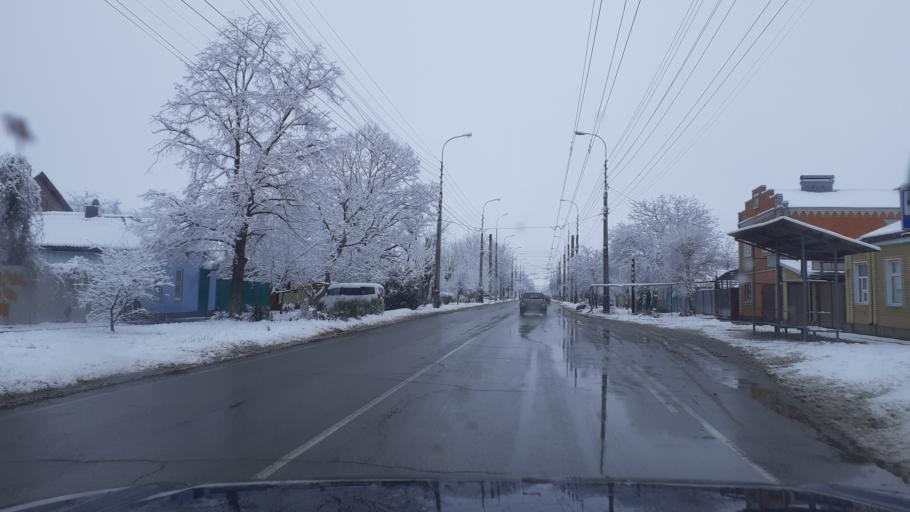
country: RU
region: Adygeya
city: Maykop
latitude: 44.6146
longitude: 40.1182
